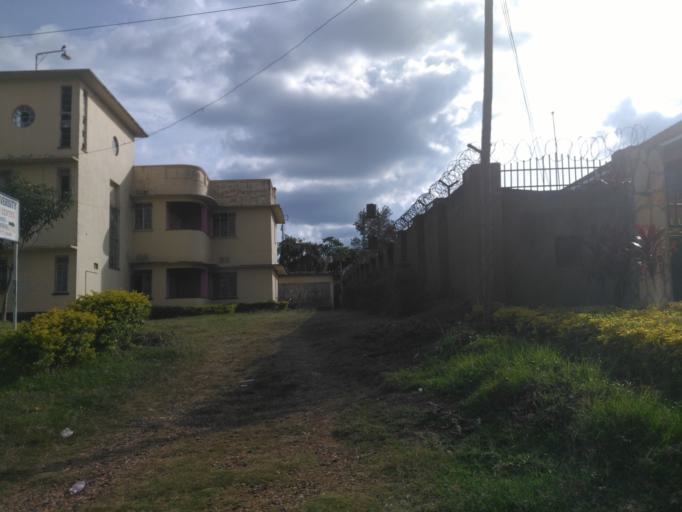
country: UG
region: Eastern Region
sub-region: Jinja District
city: Jinja
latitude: 0.4235
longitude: 33.2040
